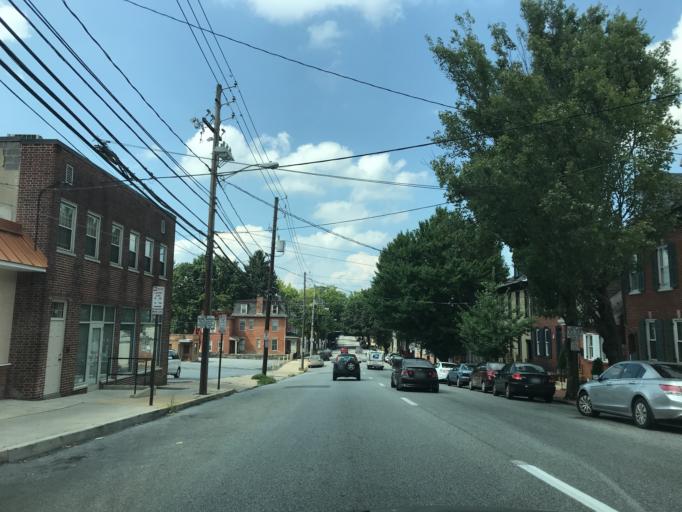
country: US
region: Pennsylvania
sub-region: Lancaster County
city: Lancaster
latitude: 40.0416
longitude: -76.3020
